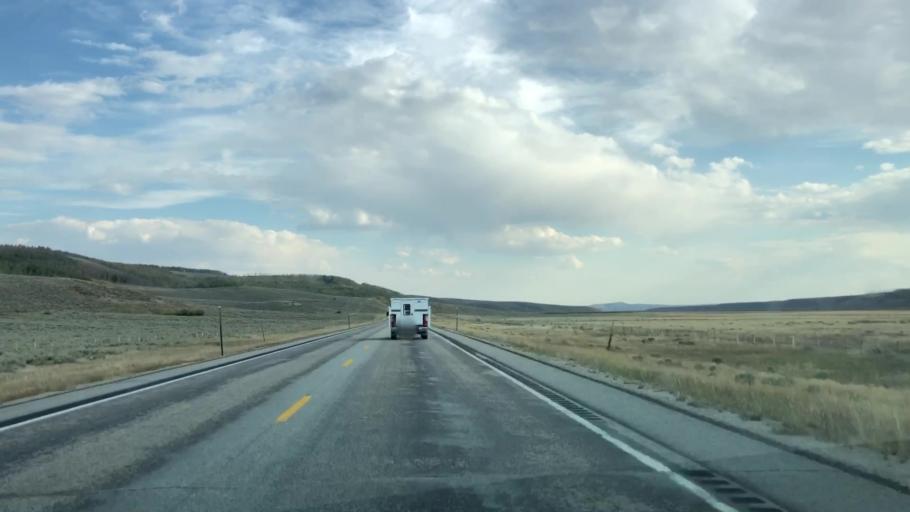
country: US
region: Wyoming
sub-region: Sublette County
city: Pinedale
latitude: 43.1005
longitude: -110.1691
